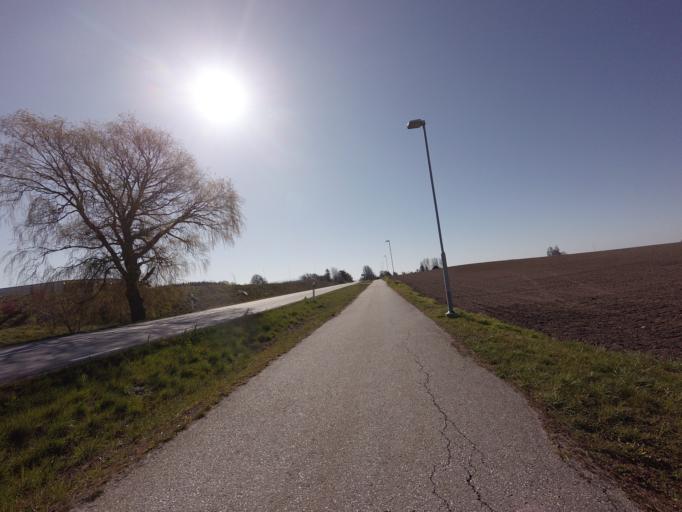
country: SE
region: Skane
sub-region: Malmo
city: Oxie
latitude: 55.4795
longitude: 13.1285
